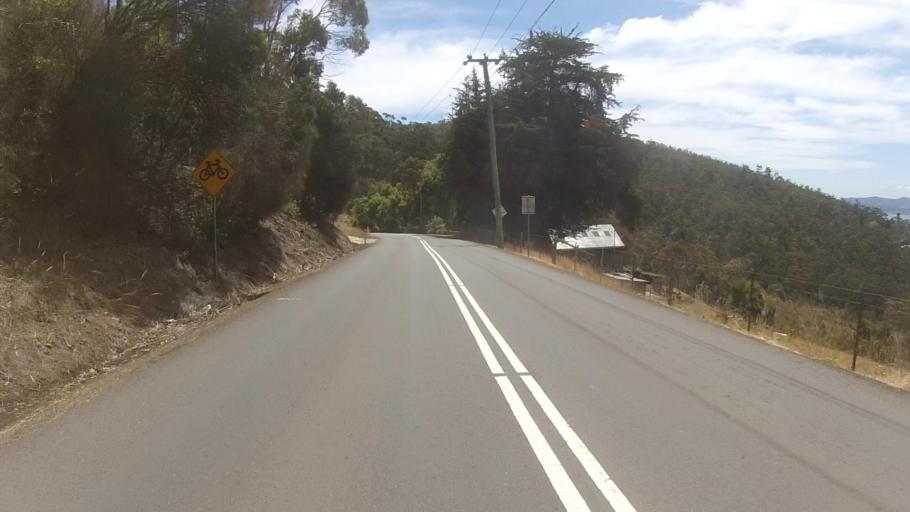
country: AU
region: Tasmania
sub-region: Kingborough
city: Kingston Beach
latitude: -42.9632
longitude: 147.3315
